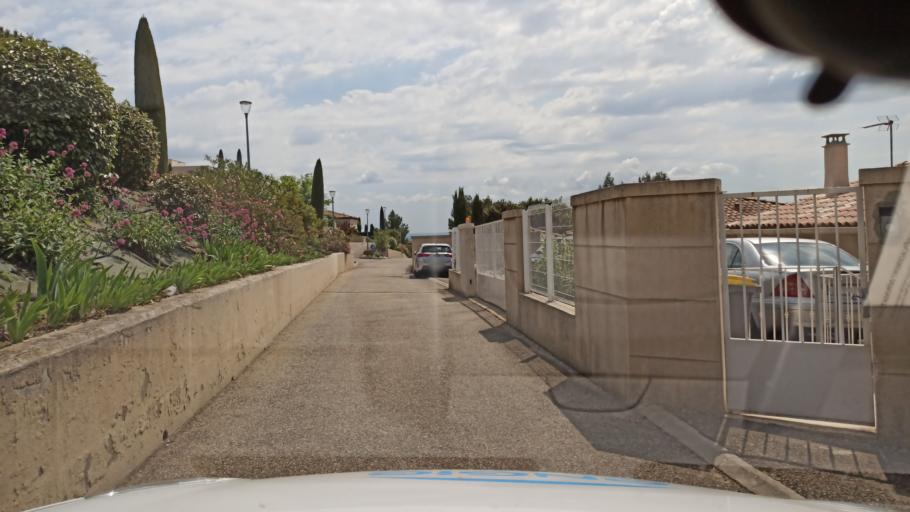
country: FR
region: Languedoc-Roussillon
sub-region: Departement du Gard
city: Les Angles
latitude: 43.9695
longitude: 4.7758
